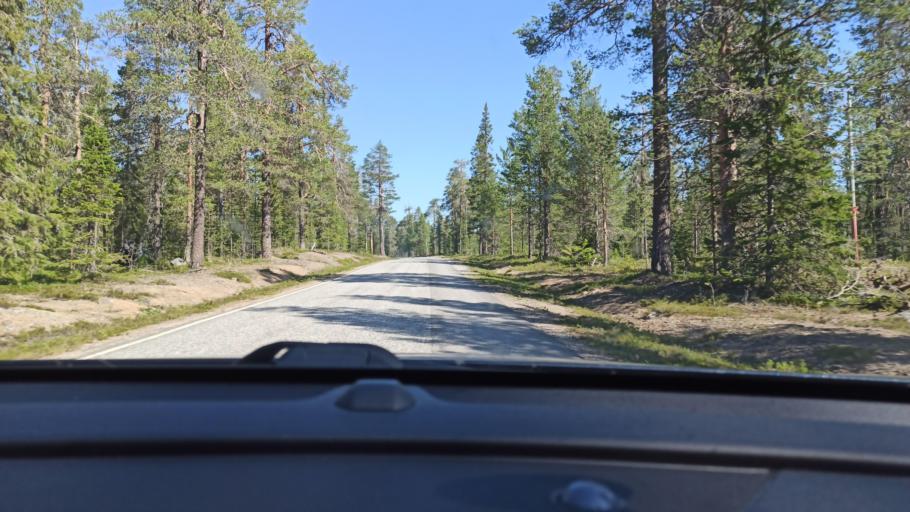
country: FI
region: Lapland
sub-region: Tunturi-Lappi
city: Kolari
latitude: 67.6582
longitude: 24.1653
